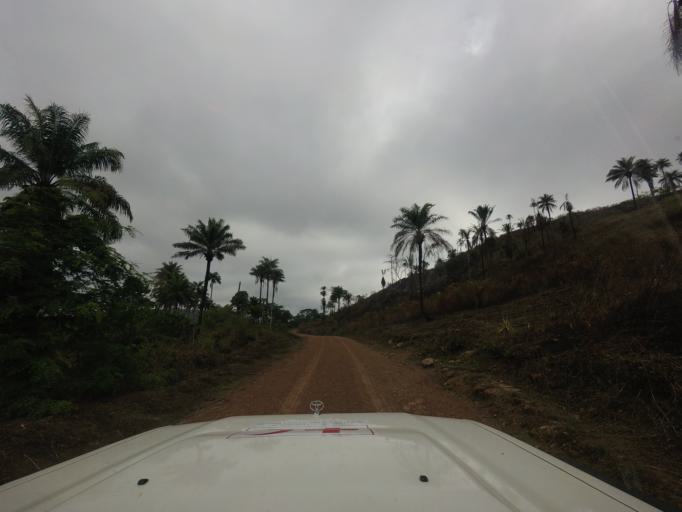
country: LR
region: Lofa
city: Voinjama
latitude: 8.4457
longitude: -9.7948
